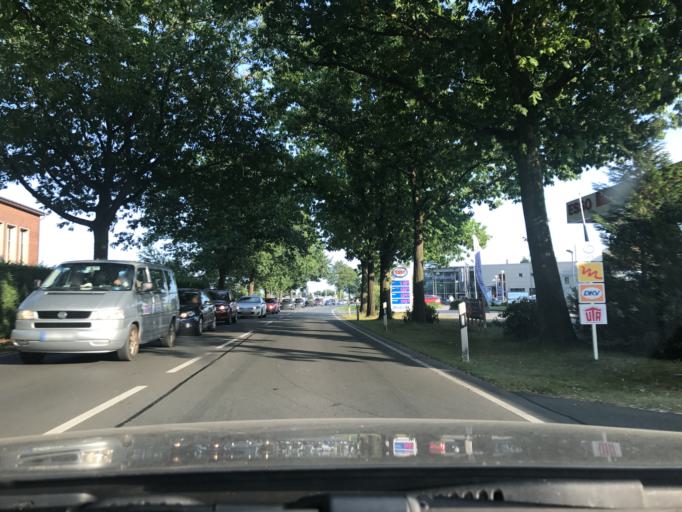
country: DE
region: North Rhine-Westphalia
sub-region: Regierungsbezirk Dusseldorf
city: Kevelaer
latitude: 51.5844
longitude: 6.2536
